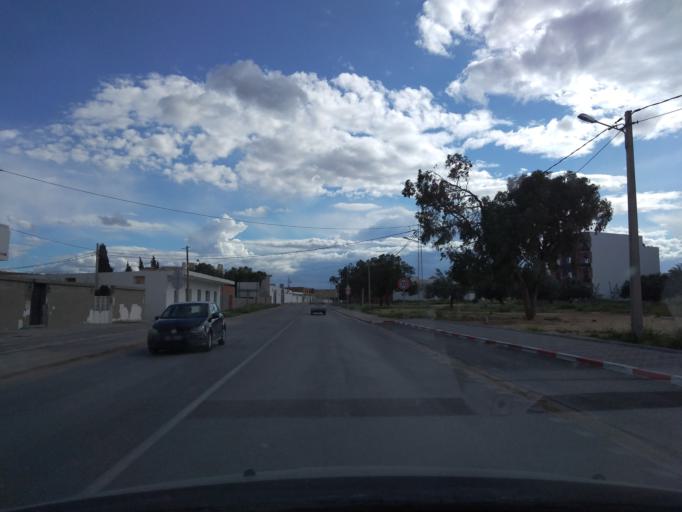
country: TN
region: Susah
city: Masakin
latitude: 35.7185
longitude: 10.5643
